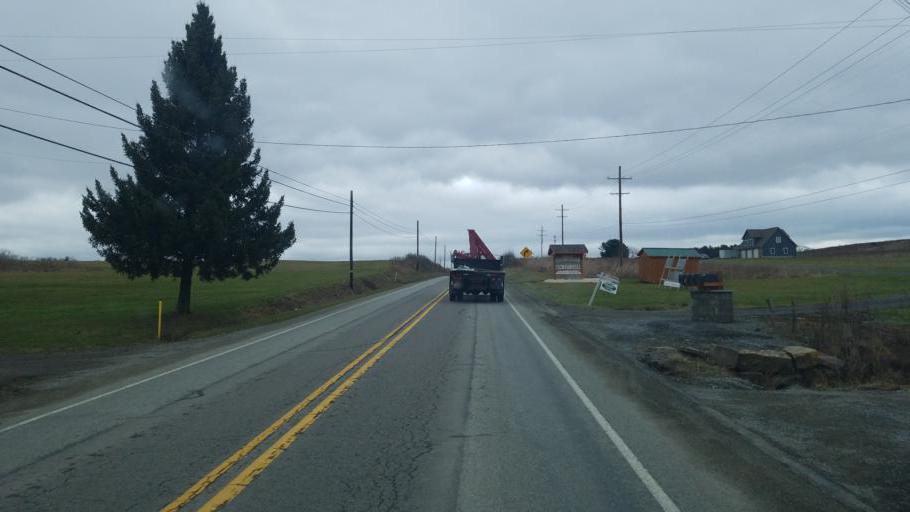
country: US
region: Pennsylvania
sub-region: Clarion County
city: Marianne
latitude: 41.3474
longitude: -79.3384
